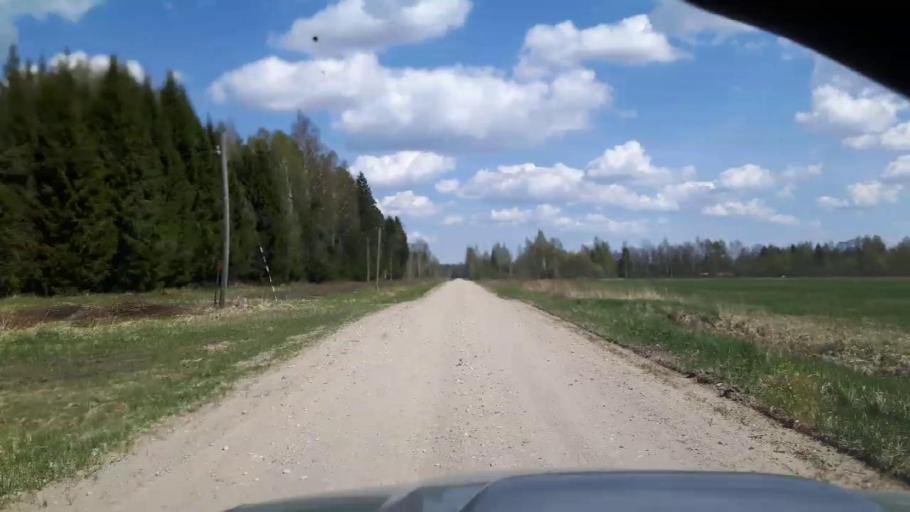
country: EE
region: Paernumaa
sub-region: Tootsi vald
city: Tootsi
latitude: 58.4670
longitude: 24.8932
